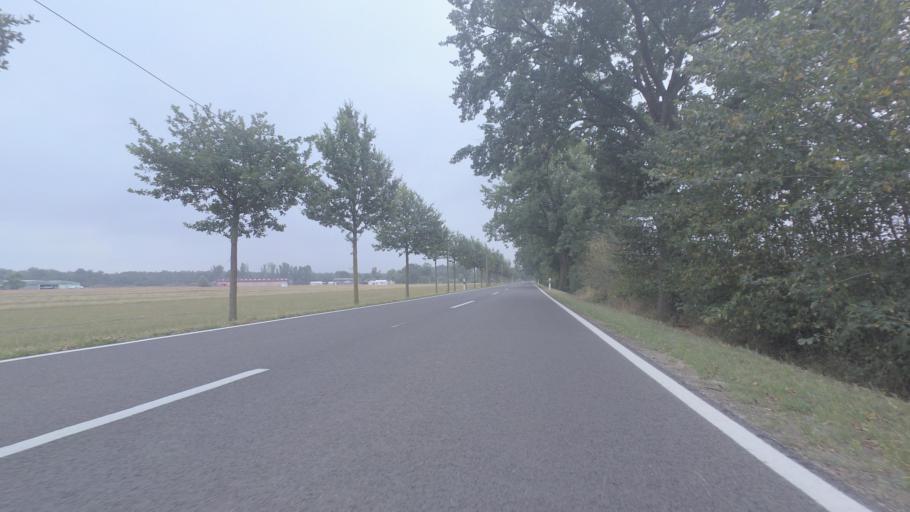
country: DE
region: Brandenburg
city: Paulinenaue
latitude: 52.6566
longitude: 12.7481
